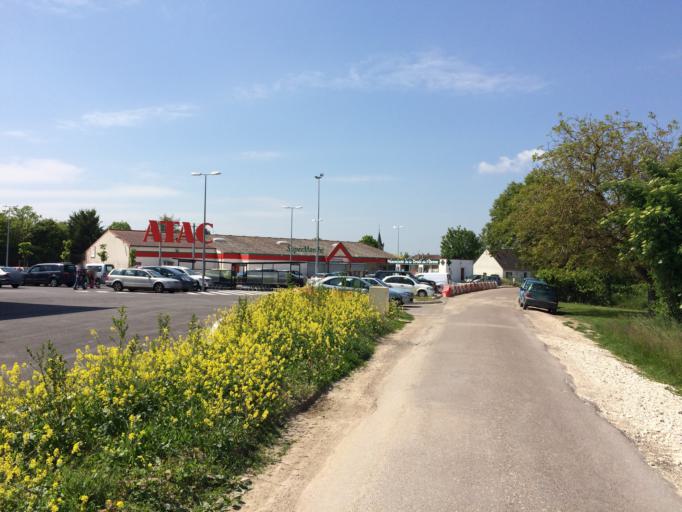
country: FR
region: Bourgogne
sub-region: Departement de l'Yonne
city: Aillant-sur-Tholon
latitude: 47.8774
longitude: 3.3537
